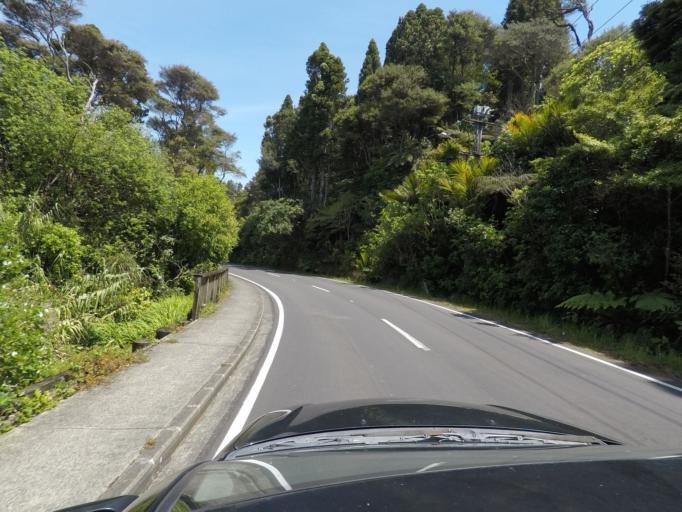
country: NZ
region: Auckland
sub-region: Auckland
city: Titirangi
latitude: -36.9608
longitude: 174.6420
